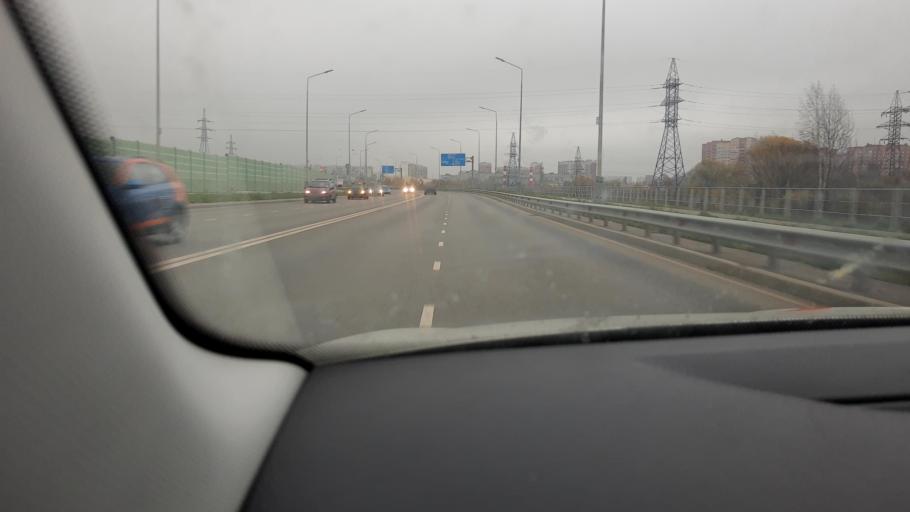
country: RU
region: Moskovskaya
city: Shcherbinka
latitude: 55.5075
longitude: 37.5458
